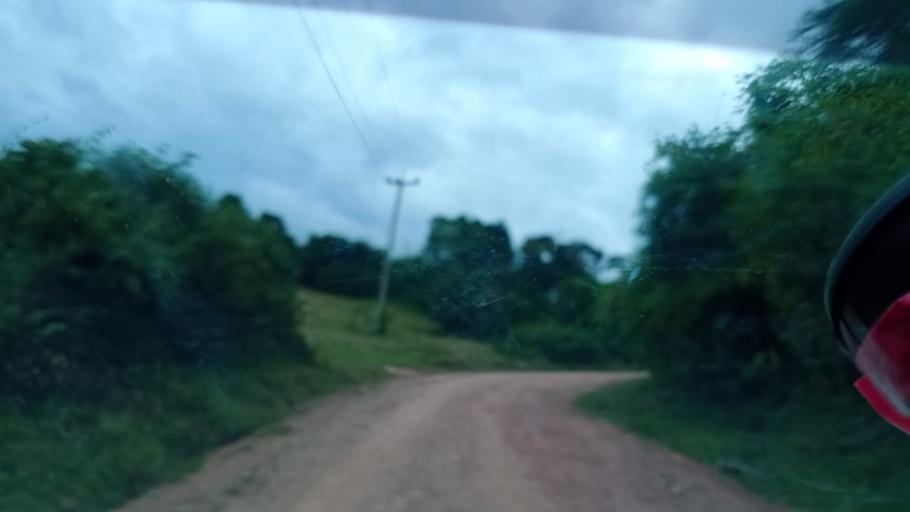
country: TH
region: Changwat Bueng Kan
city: Pak Khat
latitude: 18.7157
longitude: 103.2129
